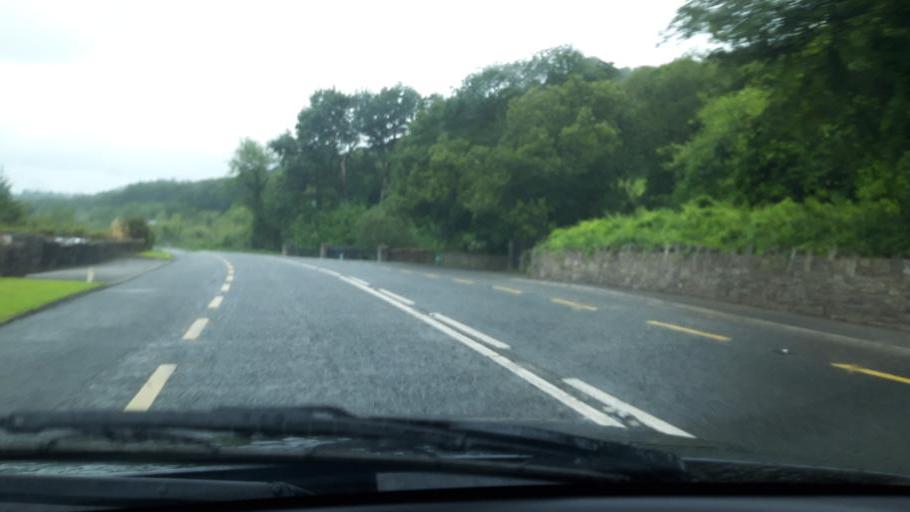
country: IE
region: Munster
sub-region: County Cork
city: Youghal
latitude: 52.1510
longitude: -7.8619
